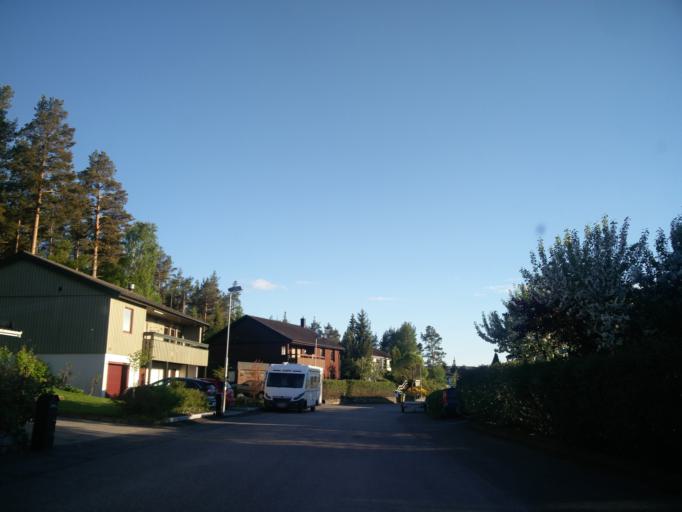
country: SE
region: Vaesternorrland
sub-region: Sundsvalls Kommun
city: Sundsvall
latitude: 62.4053
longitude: 17.2755
